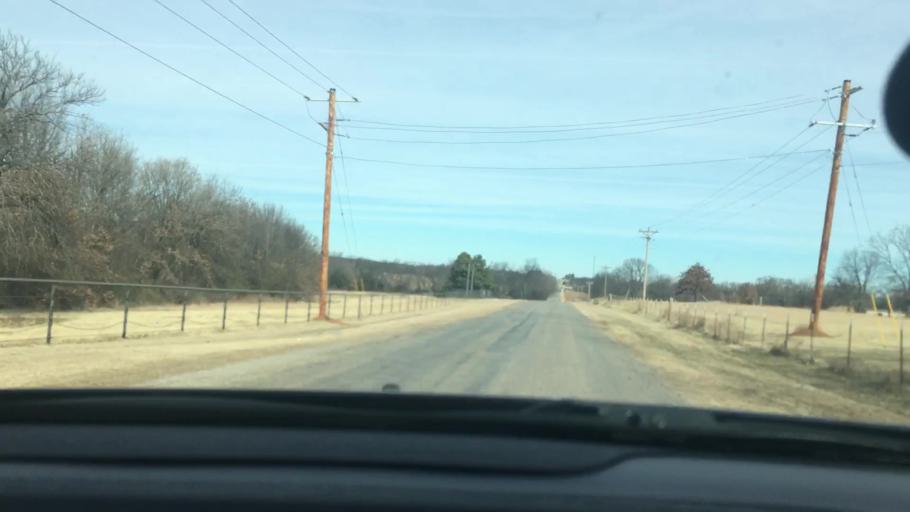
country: US
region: Oklahoma
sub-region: Garvin County
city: Wynnewood
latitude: 34.6377
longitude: -97.2475
